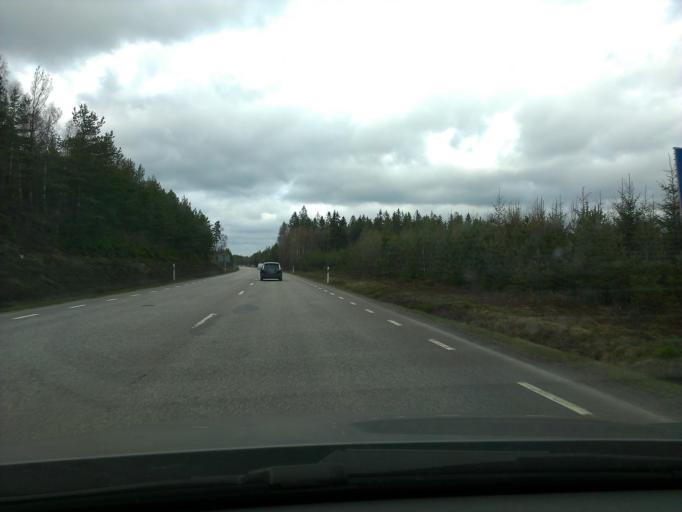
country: SE
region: Kronoberg
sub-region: Almhults Kommun
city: AElmhult
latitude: 56.5648
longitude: 14.1833
